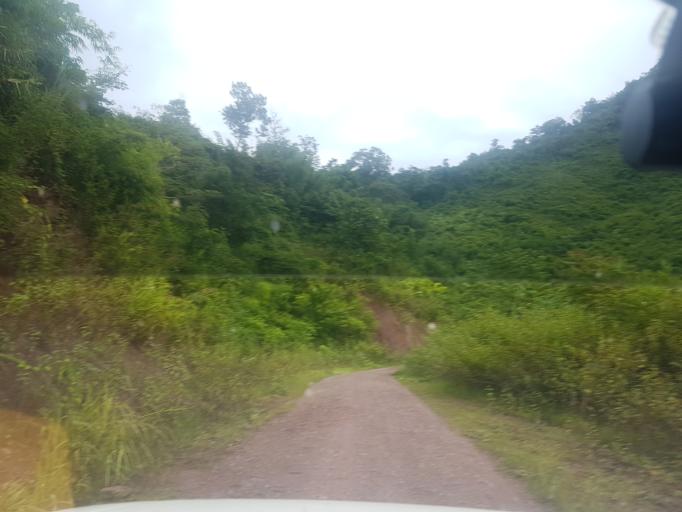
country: LA
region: Xiangkhoang
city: Phonsavan
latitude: 19.7532
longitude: 103.0509
